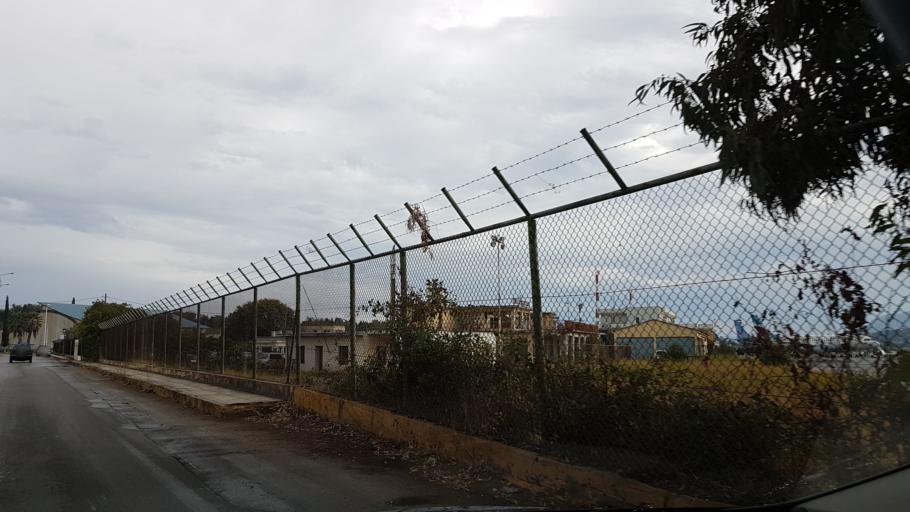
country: GR
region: Ionian Islands
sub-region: Nomos Kerkyras
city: Kerkyra
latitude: 39.6124
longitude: 19.9116
